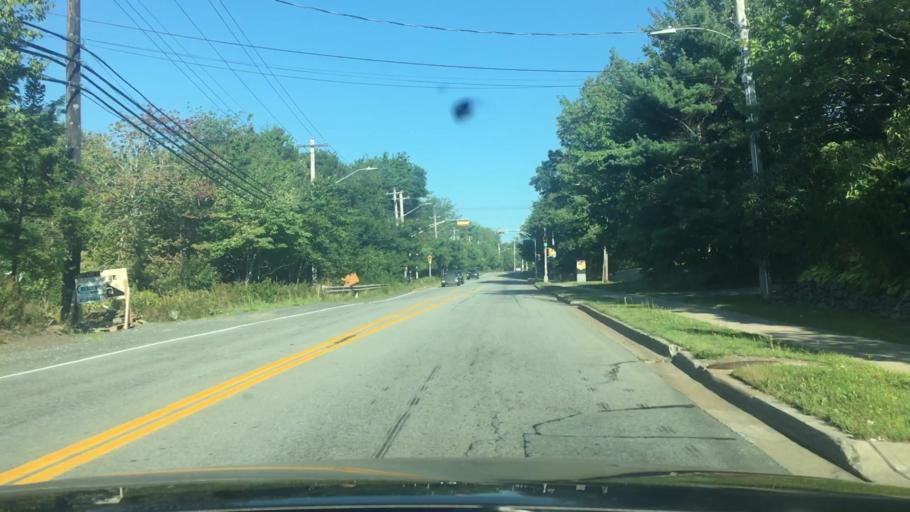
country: CA
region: Nova Scotia
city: Dartmouth
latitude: 44.7165
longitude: -63.6821
